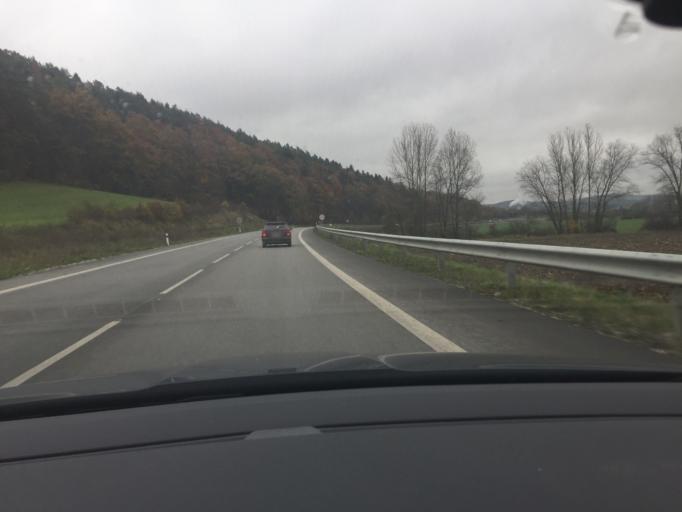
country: SK
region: Presovsky
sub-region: Okres Bardejov
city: Bardejov
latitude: 49.3059
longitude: 21.2260
